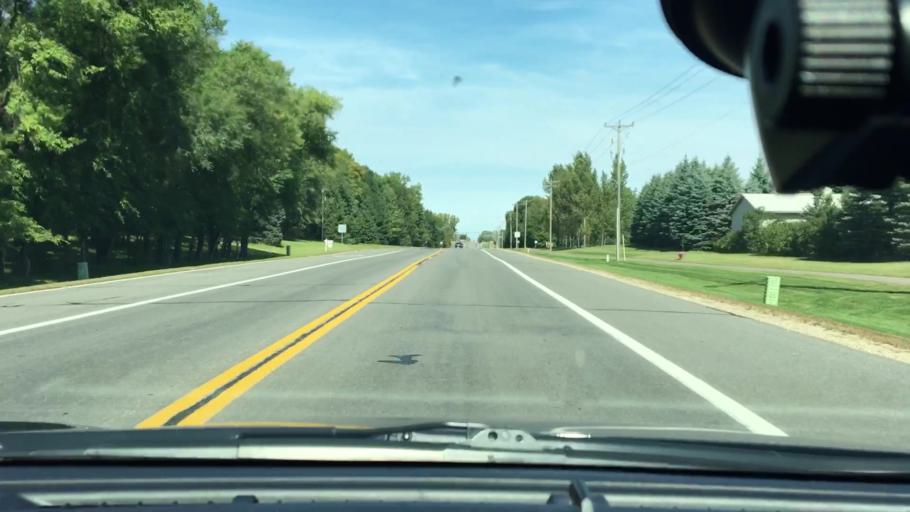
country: US
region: Minnesota
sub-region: Wright County
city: Hanover
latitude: 45.1662
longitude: -93.6659
